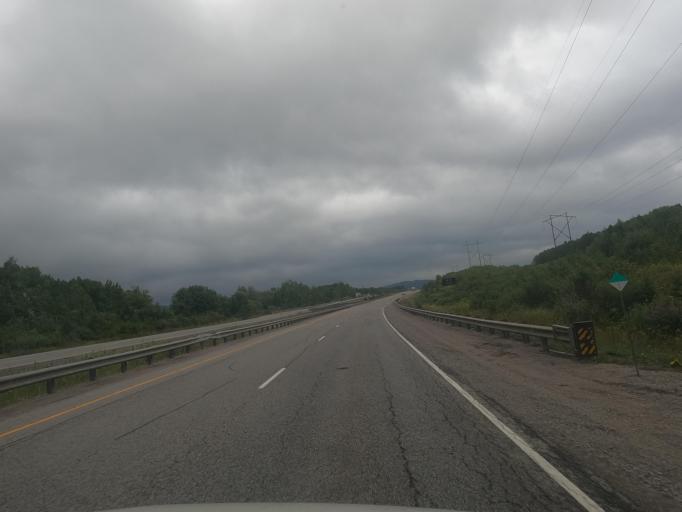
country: CA
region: Ontario
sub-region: Algoma
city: Sault Ste. Marie
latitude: 46.5575
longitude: -84.2178
